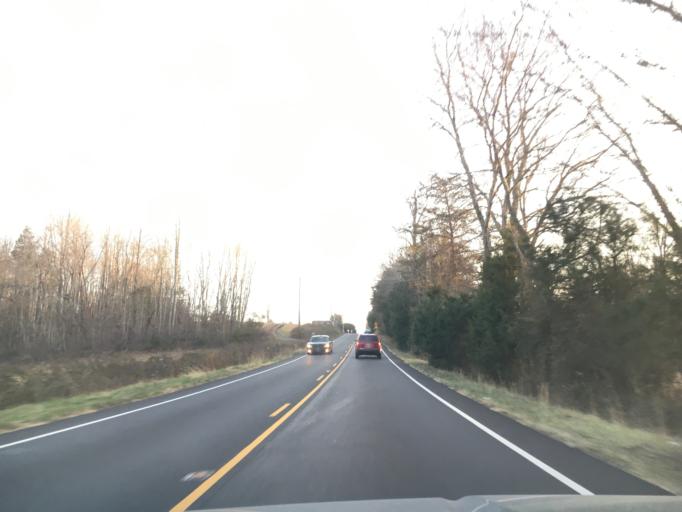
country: US
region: Virginia
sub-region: Orange County
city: Orange
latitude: 38.2428
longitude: -77.9520
